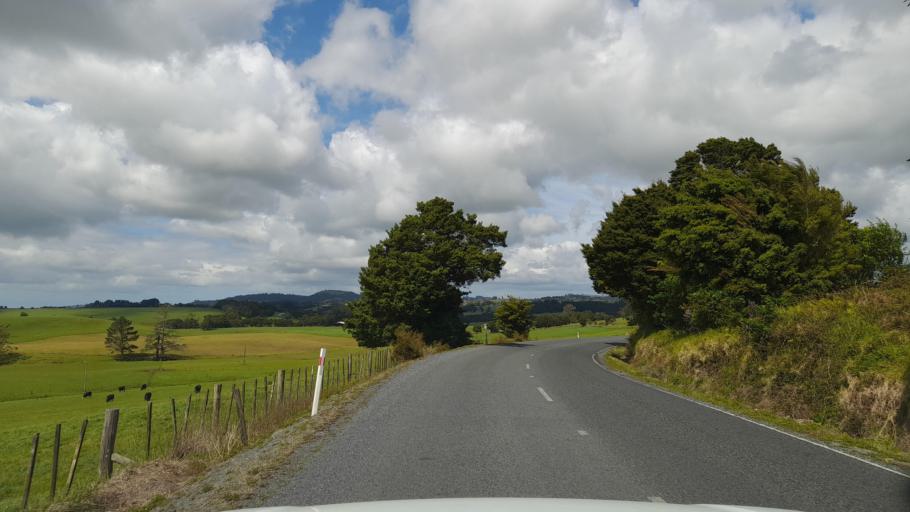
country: NZ
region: Northland
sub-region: Whangarei
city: Maungatapere
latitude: -35.6517
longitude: 174.1236
